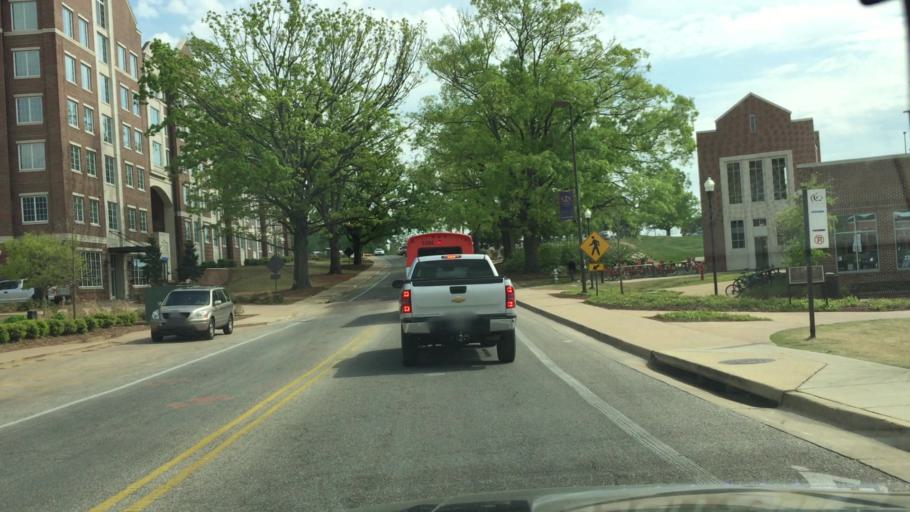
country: US
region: Alabama
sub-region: Lee County
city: Auburn
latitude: 32.5991
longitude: -85.4905
